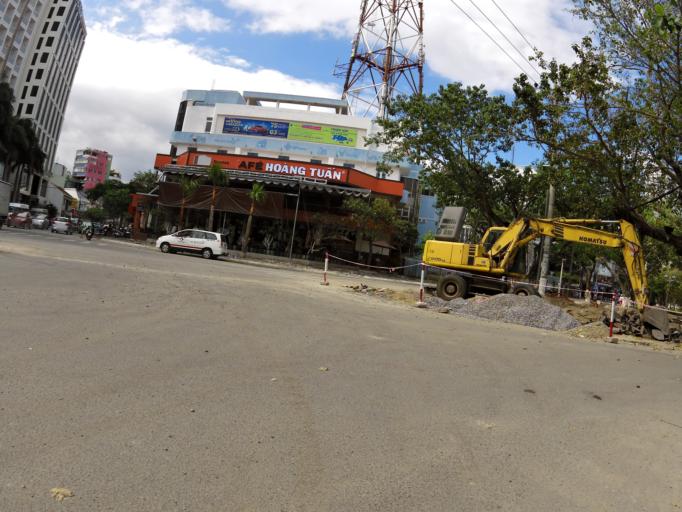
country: VN
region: Khanh Hoa
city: Nha Trang
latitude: 12.2535
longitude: 109.1958
